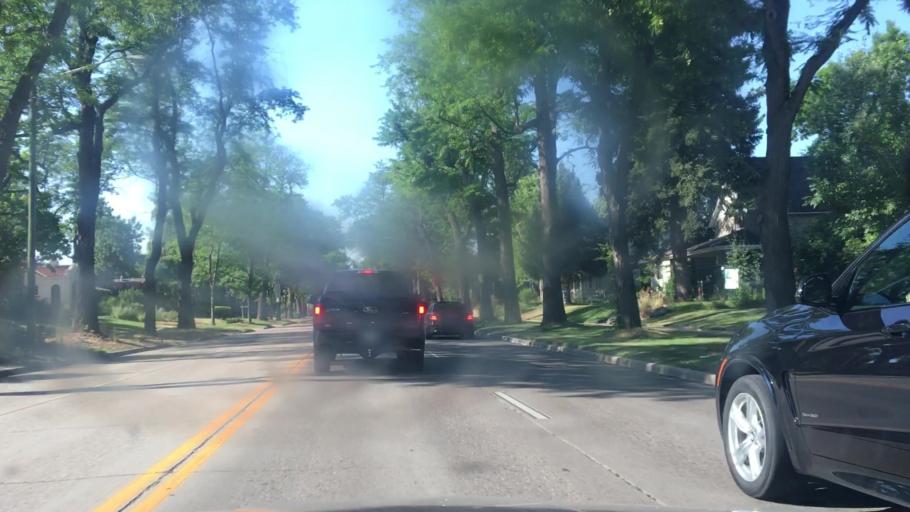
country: US
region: Colorado
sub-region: Arapahoe County
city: Glendale
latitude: 39.6981
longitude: -104.9593
